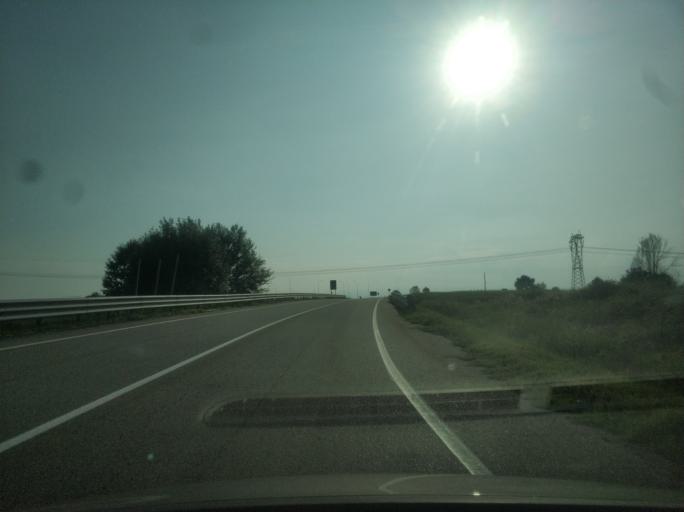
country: IT
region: Piedmont
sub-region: Provincia di Cuneo
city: Roreto
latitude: 44.6633
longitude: 7.8200
